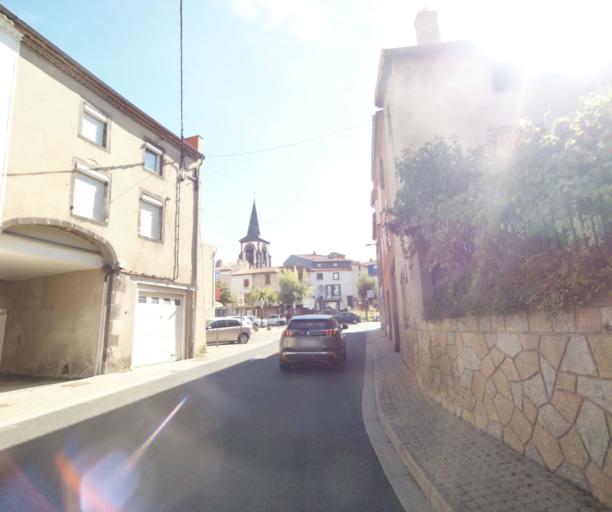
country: FR
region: Auvergne
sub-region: Departement du Puy-de-Dome
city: Cournon-d'Auvergne
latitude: 45.7706
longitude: 3.1969
